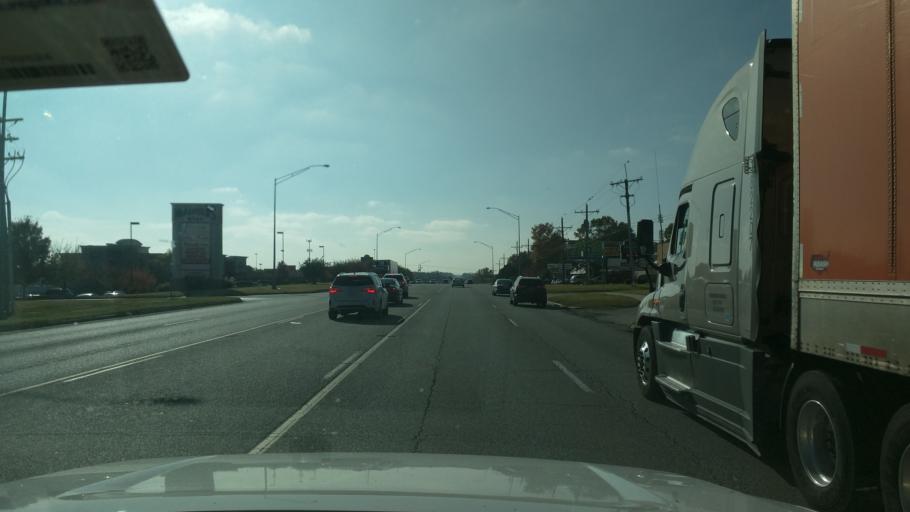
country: US
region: Oklahoma
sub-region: Washington County
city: Bartlesville
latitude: 36.7176
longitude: -95.9352
